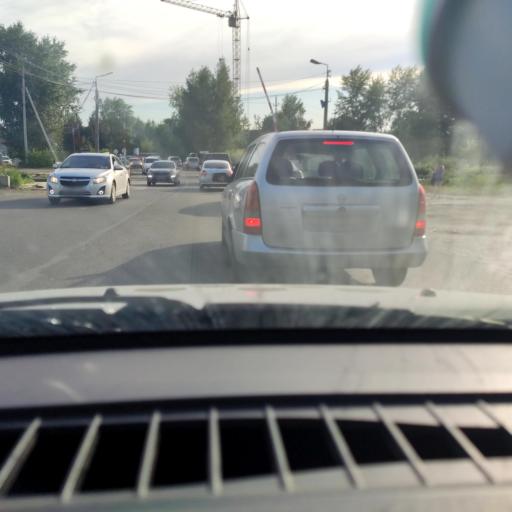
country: RU
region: Kirov
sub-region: Kirovo-Chepetskiy Rayon
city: Kirov
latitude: 58.6211
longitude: 49.6357
